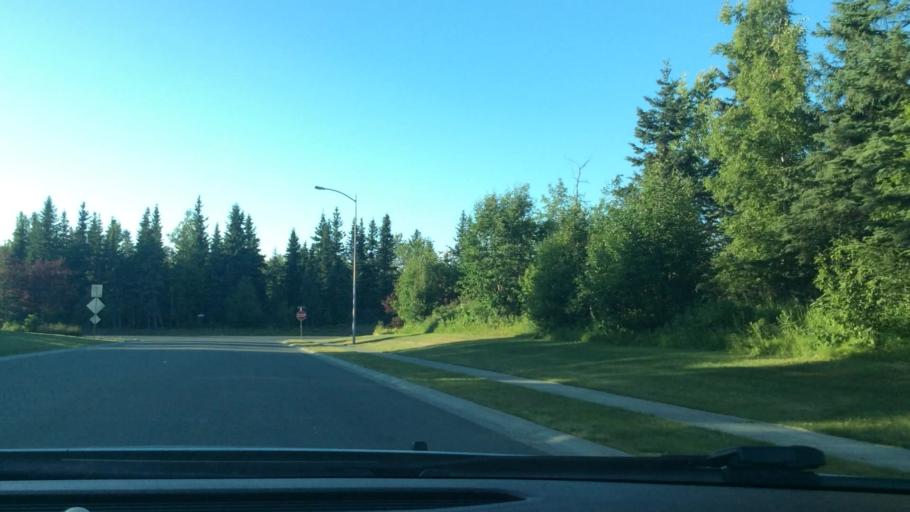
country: US
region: Alaska
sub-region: Anchorage Municipality
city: Elmendorf Air Force Base
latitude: 61.2391
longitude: -149.7239
